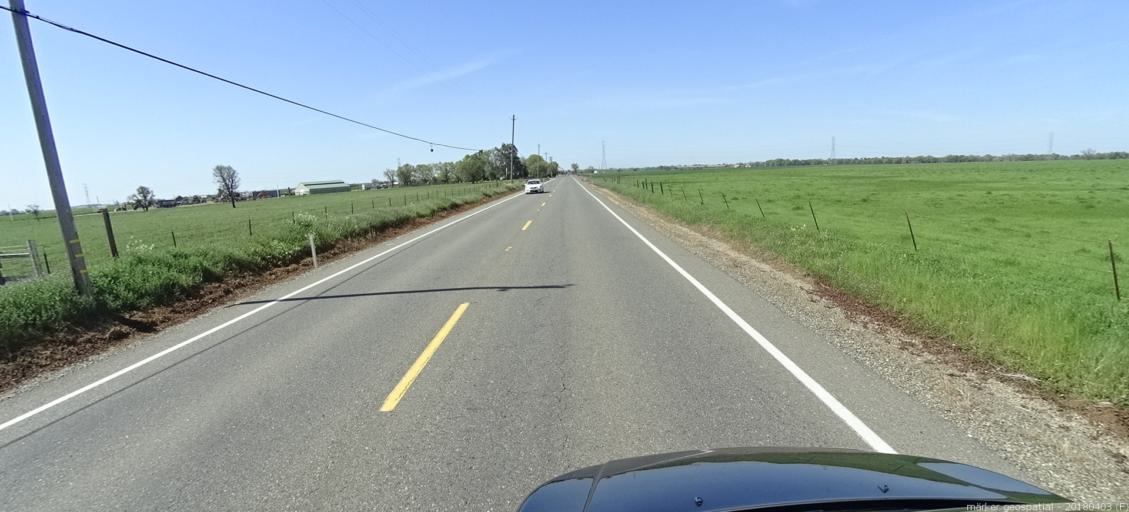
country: US
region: California
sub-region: Sacramento County
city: Wilton
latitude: 38.3887
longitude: -121.2785
